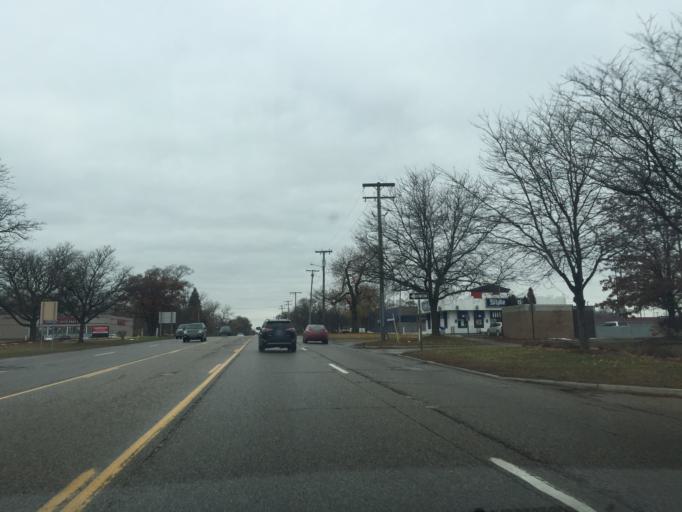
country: US
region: Michigan
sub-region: Oakland County
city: Farmington
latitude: 42.4419
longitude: -83.3225
